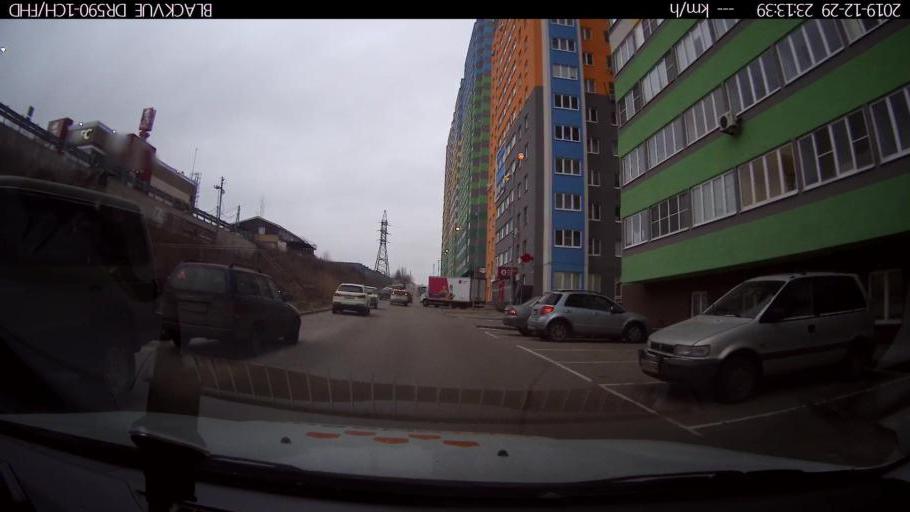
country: RU
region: Nizjnij Novgorod
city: Afonino
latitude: 56.2770
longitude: 44.0842
